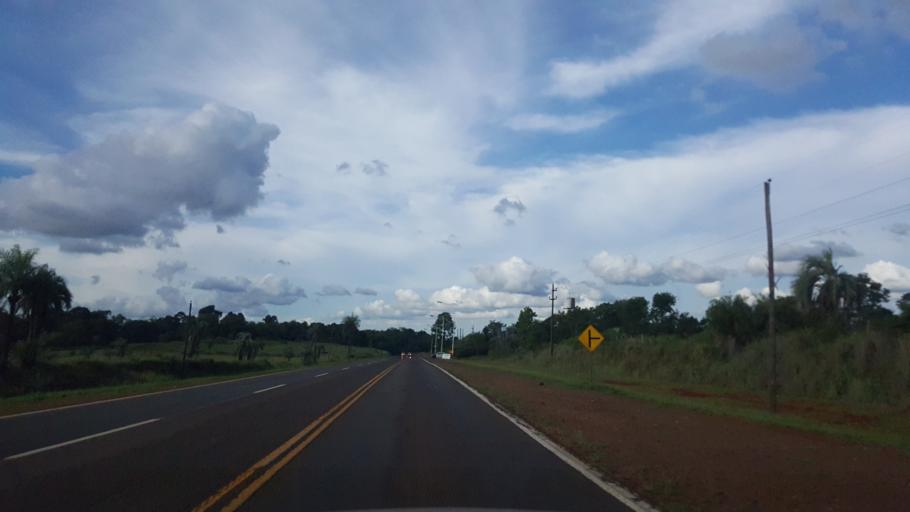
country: AR
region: Misiones
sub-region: Departamento de Candelaria
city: Loreto
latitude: -27.3381
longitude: -55.5448
